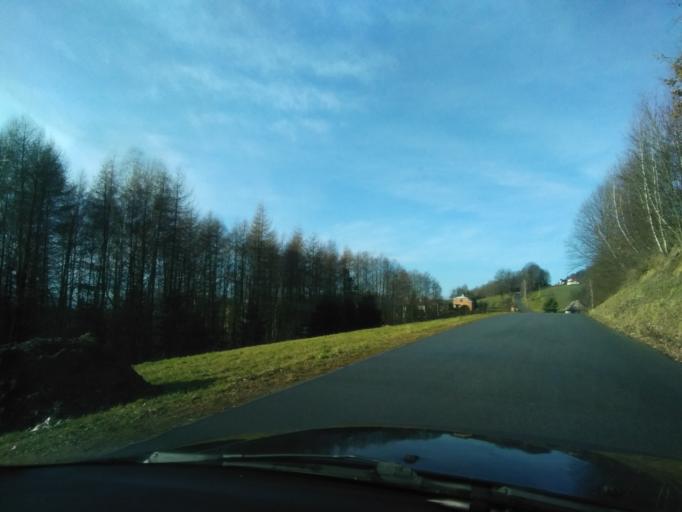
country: PL
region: Subcarpathian Voivodeship
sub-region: Powiat krosnienski
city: Korczyna
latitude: 49.7231
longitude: 21.8035
